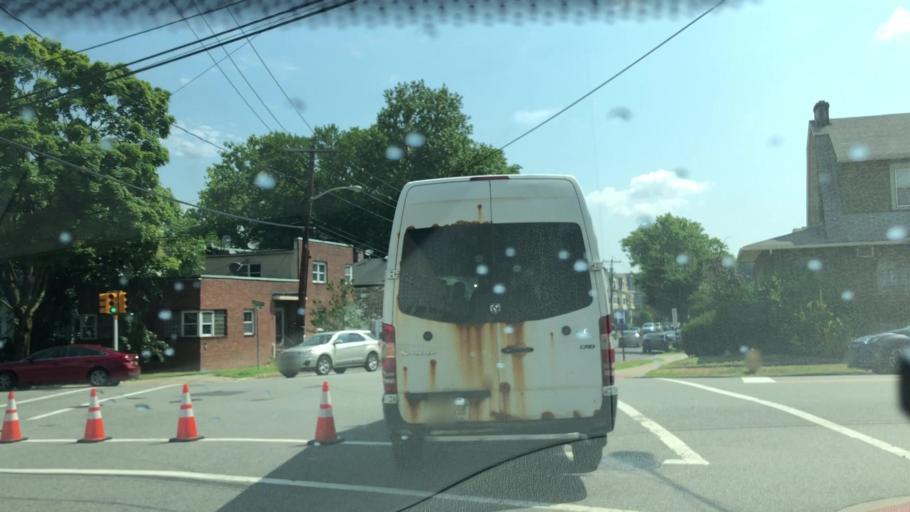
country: US
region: New Jersey
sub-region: Essex County
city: Glen Ridge
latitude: 40.7890
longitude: -74.1941
